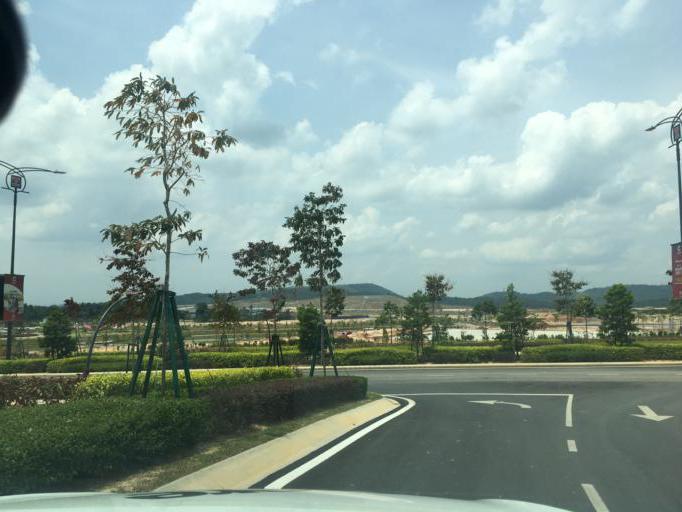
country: MY
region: Putrajaya
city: Putrajaya
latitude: 2.8440
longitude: 101.6959
